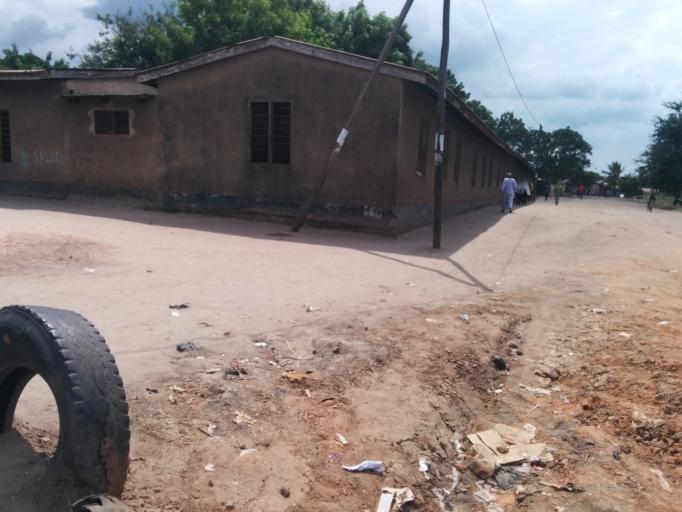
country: TZ
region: Dar es Salaam
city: Dar es Salaam
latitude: -6.8632
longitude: 39.2560
